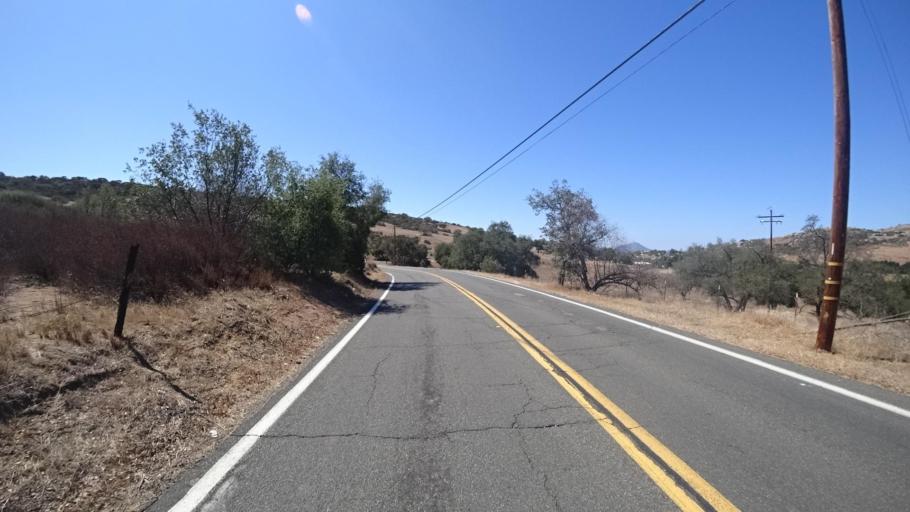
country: US
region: California
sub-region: San Diego County
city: San Diego Country Estates
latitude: 33.0490
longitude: -116.8136
